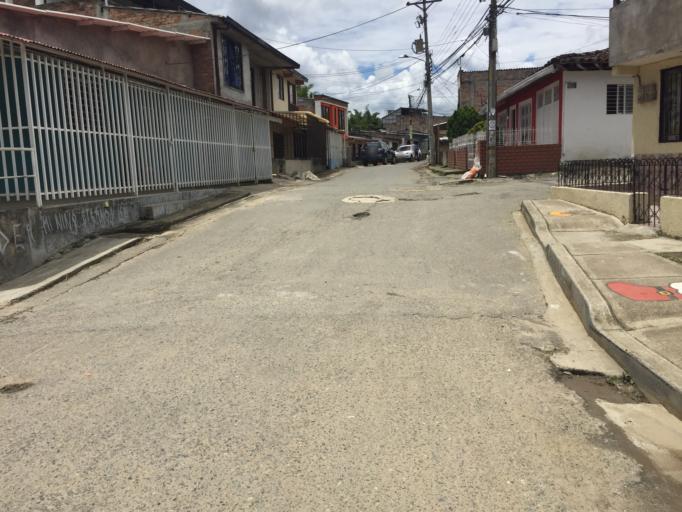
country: CO
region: Cauca
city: Popayan
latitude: 2.4573
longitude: -76.5858
